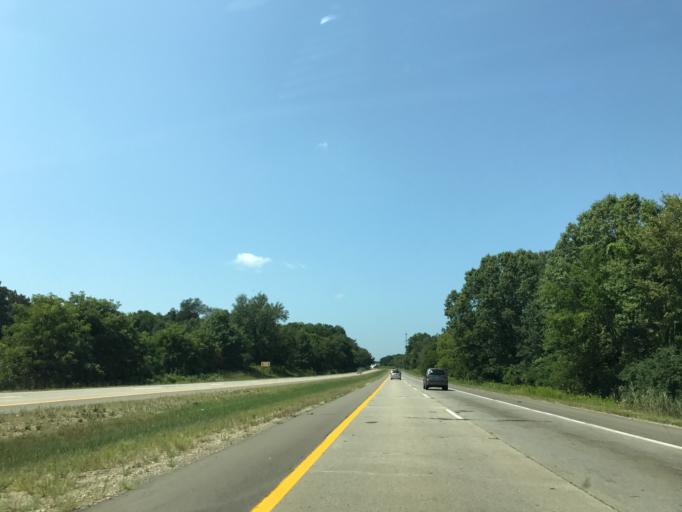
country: US
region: Michigan
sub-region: Berrien County
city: Niles
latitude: 41.8026
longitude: -86.2847
